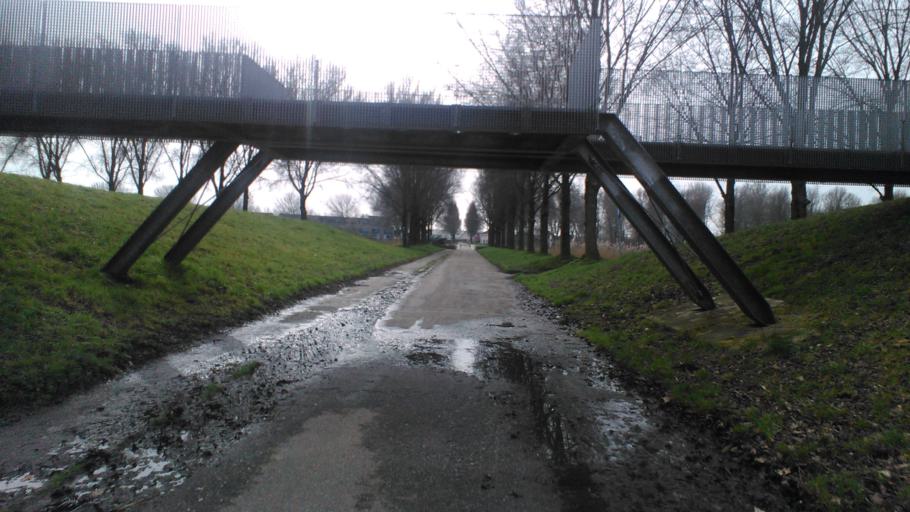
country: NL
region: South Holland
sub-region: Gemeente Pijnacker-Nootdorp
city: Pijnacker
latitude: 52.0426
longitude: 4.4588
